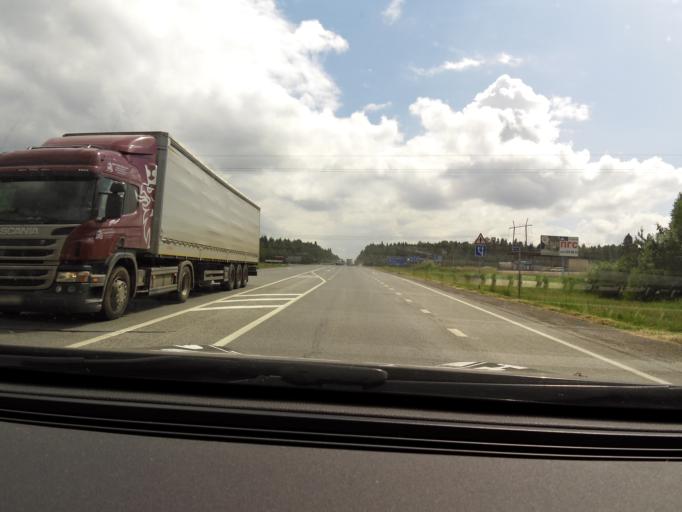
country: RU
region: Perm
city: Kungur
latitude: 57.3288
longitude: 56.9559
